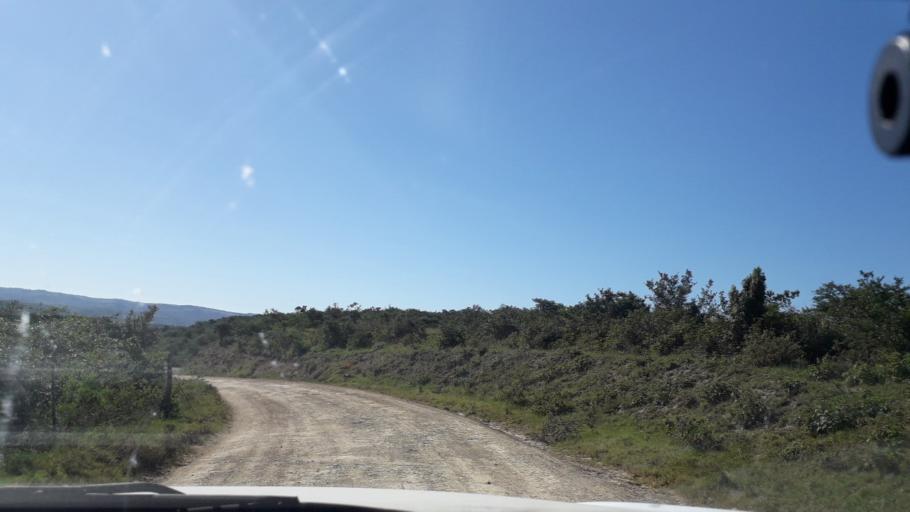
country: ZA
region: Eastern Cape
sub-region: Amathole District Municipality
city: Komga
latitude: -32.7819
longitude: 27.9571
